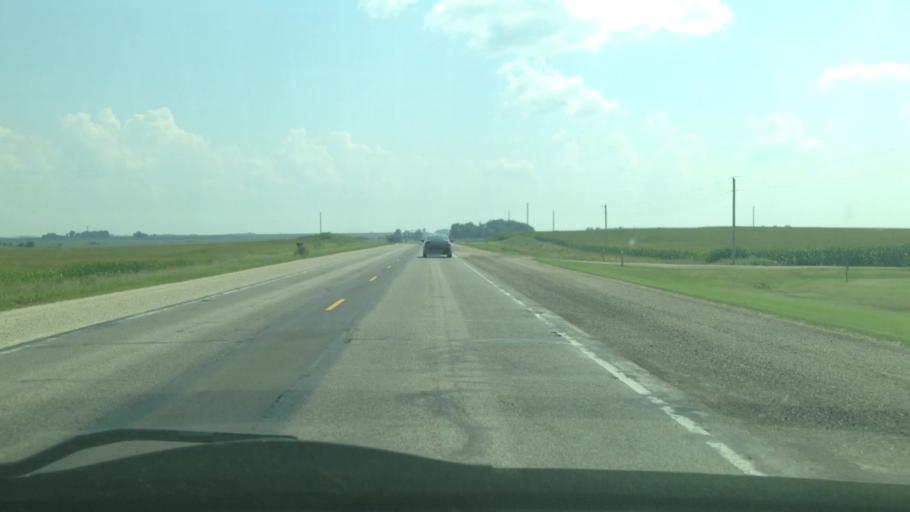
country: US
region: Iowa
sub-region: Howard County
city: Cresco
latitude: 43.3520
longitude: -92.2986
